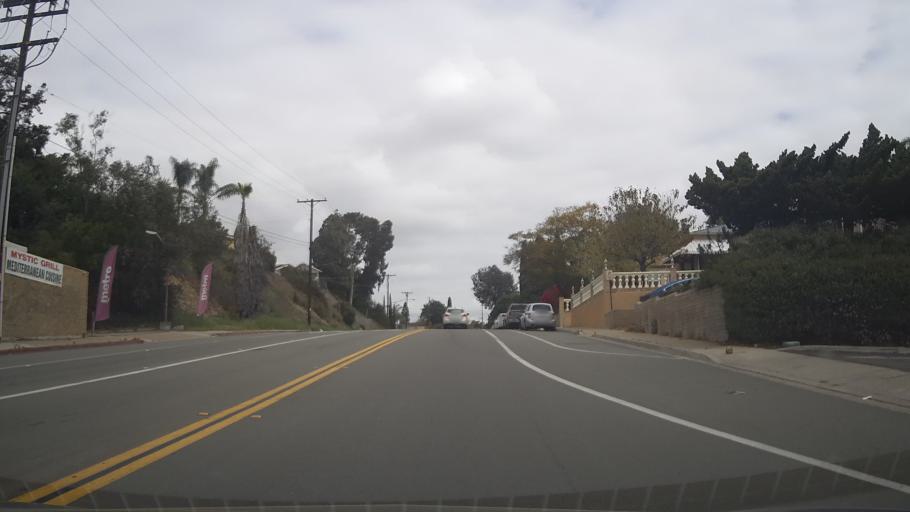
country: US
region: California
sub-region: San Diego County
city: Lemon Grove
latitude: 32.7564
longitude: -117.0478
